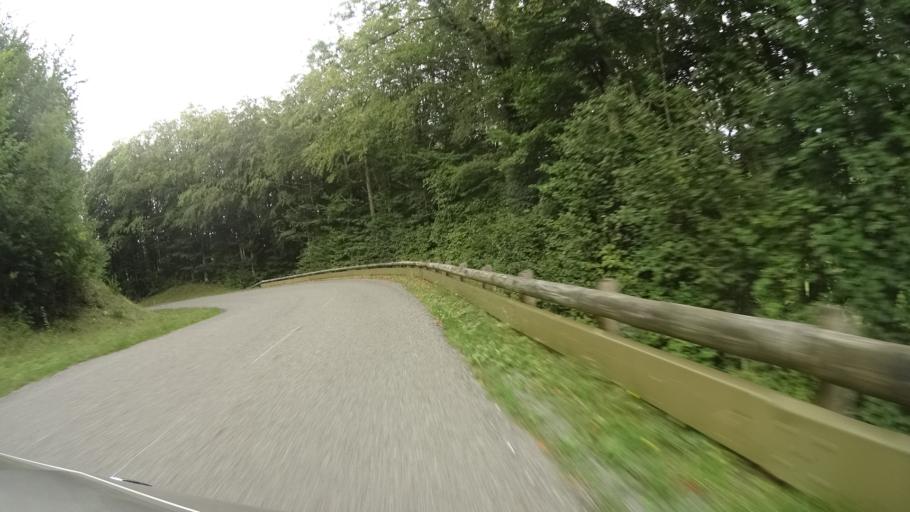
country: FR
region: Franche-Comte
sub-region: Departement du Jura
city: Morbier
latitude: 46.6329
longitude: 6.0220
